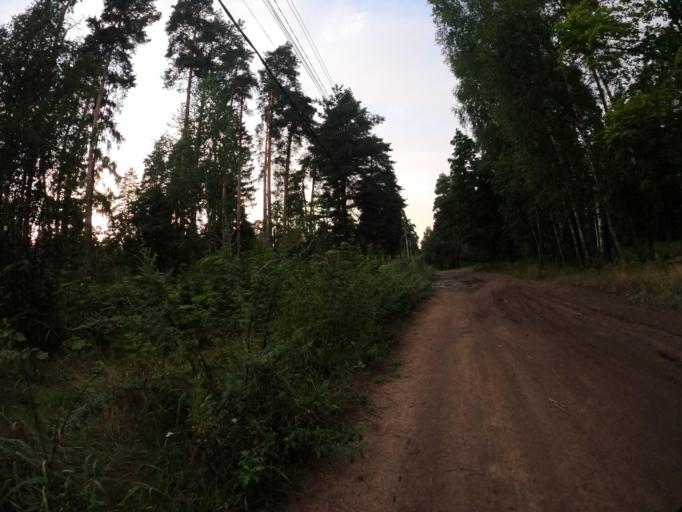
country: RU
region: Moskovskaya
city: Rodniki
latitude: 55.6414
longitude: 38.0651
